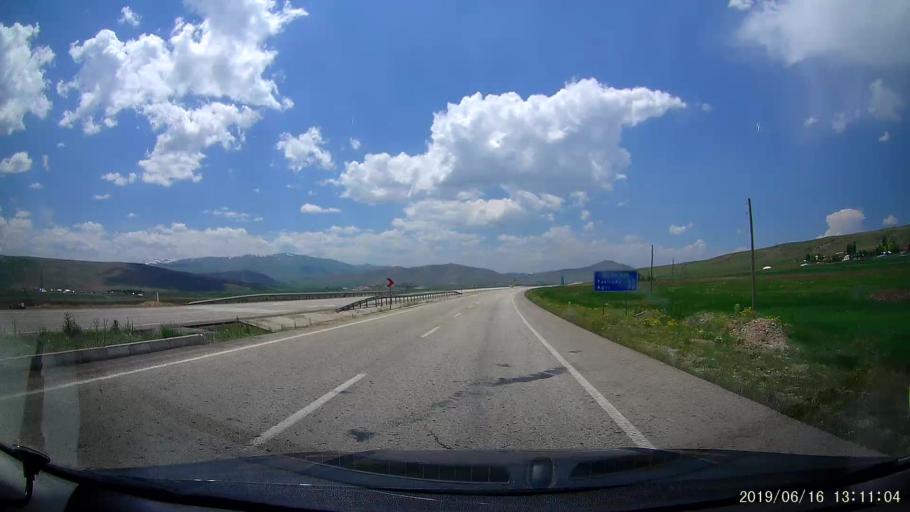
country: TR
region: Agri
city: Diyadin
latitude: 39.5910
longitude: 43.6174
